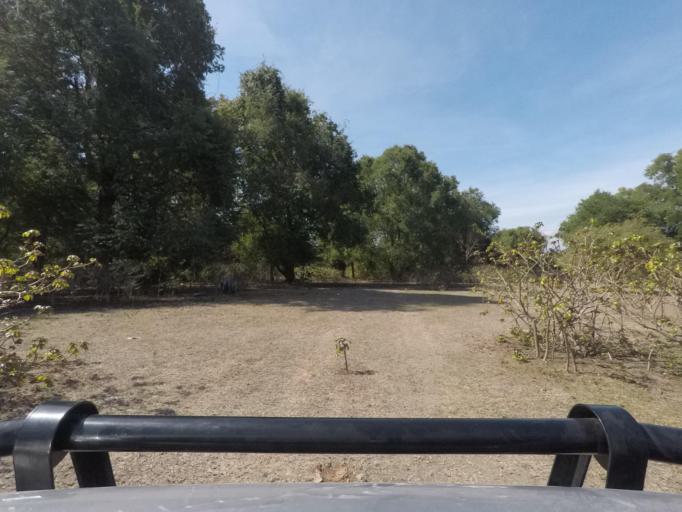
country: TL
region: Bobonaro
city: Maliana
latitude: -8.8796
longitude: 125.0078
